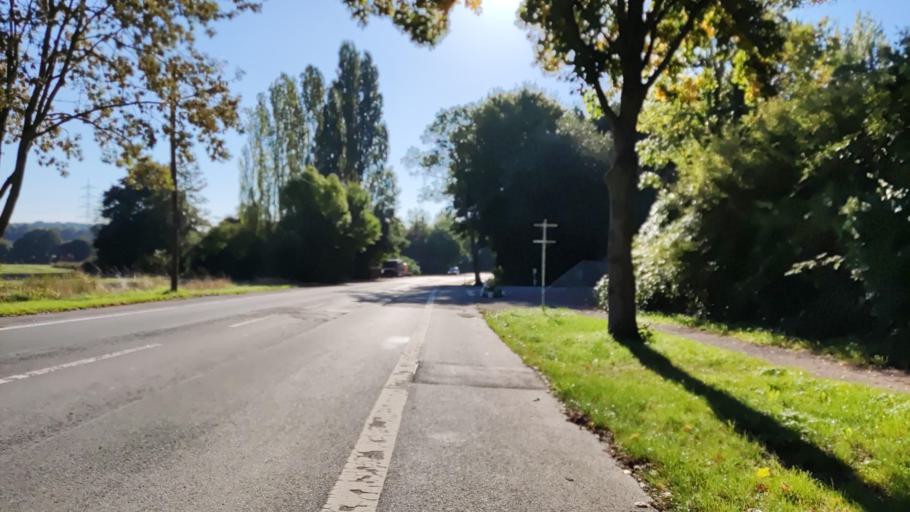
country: DE
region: North Rhine-Westphalia
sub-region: Regierungsbezirk Arnsberg
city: Bochum
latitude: 51.4660
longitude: 7.2782
